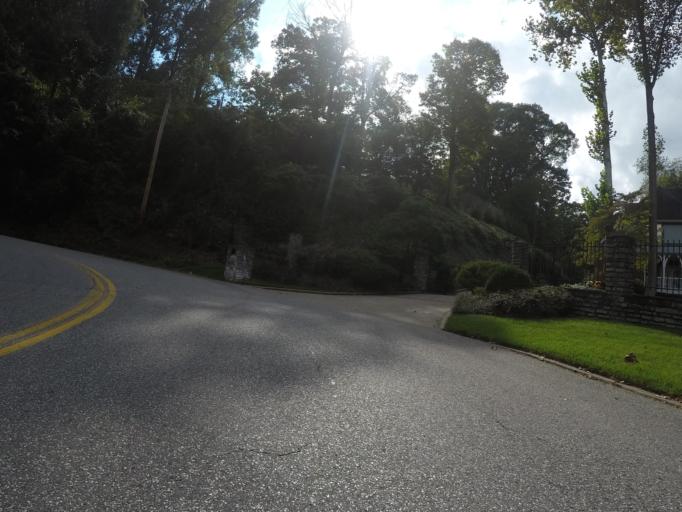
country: US
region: West Virginia
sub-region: Cabell County
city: Huntington
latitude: 38.4045
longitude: -82.4402
